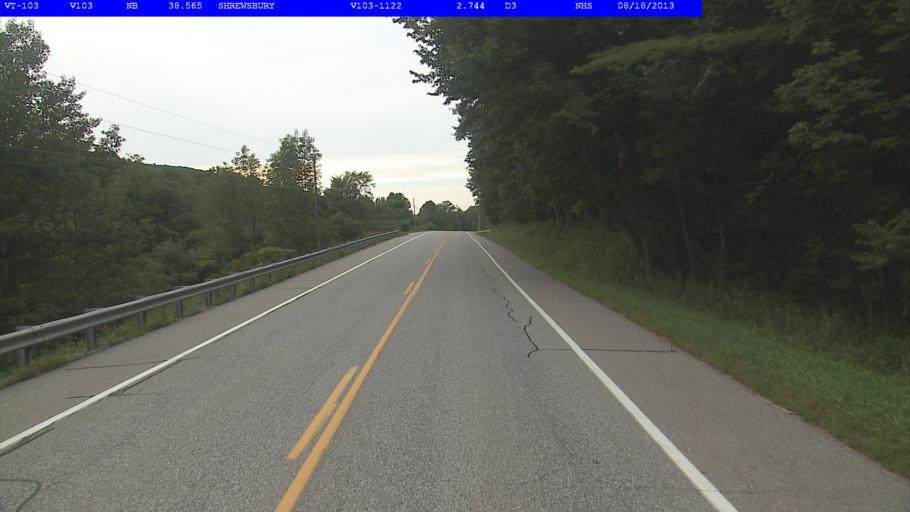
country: US
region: Vermont
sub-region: Rutland County
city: Rutland
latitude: 43.5097
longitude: -72.9094
